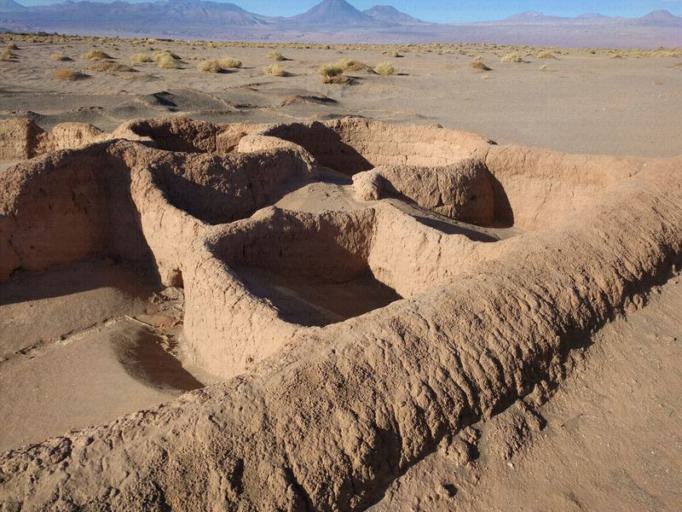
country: CL
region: Antofagasta
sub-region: Provincia de El Loa
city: San Pedro de Atacama
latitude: -22.9686
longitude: -68.2425
